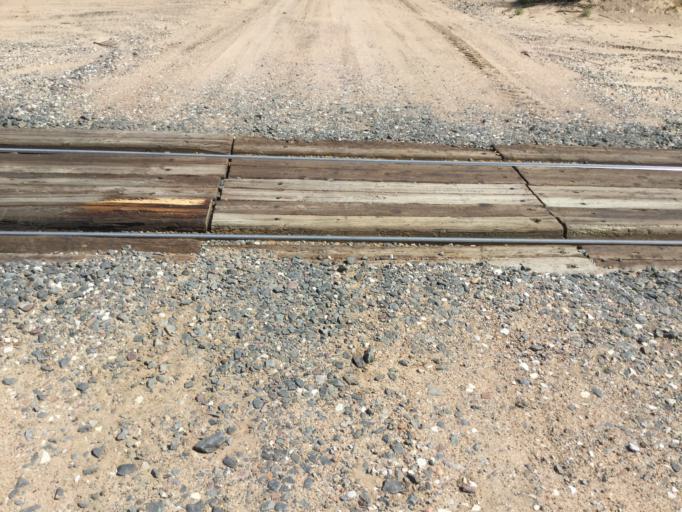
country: US
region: Kansas
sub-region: Pawnee County
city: Larned
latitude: 37.9485
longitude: -99.1507
